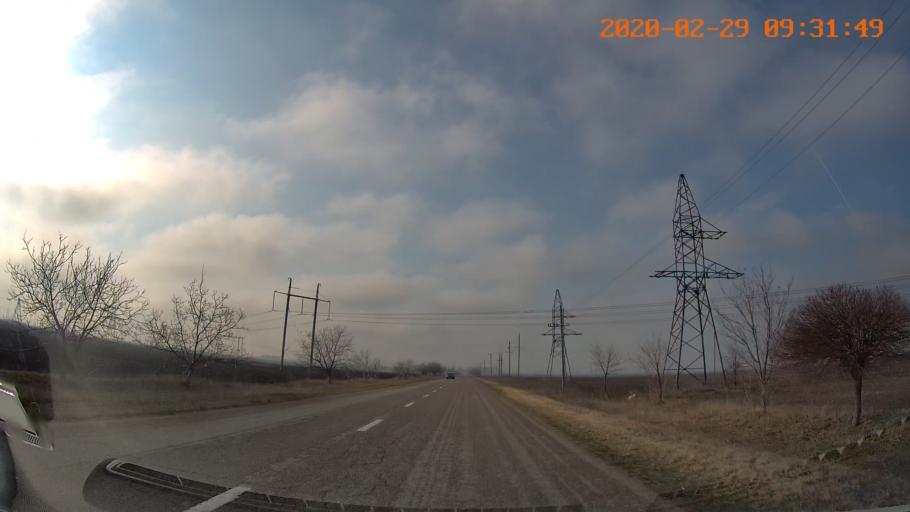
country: MD
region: Telenesti
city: Dnestrovsc
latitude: 46.6478
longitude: 29.9092
